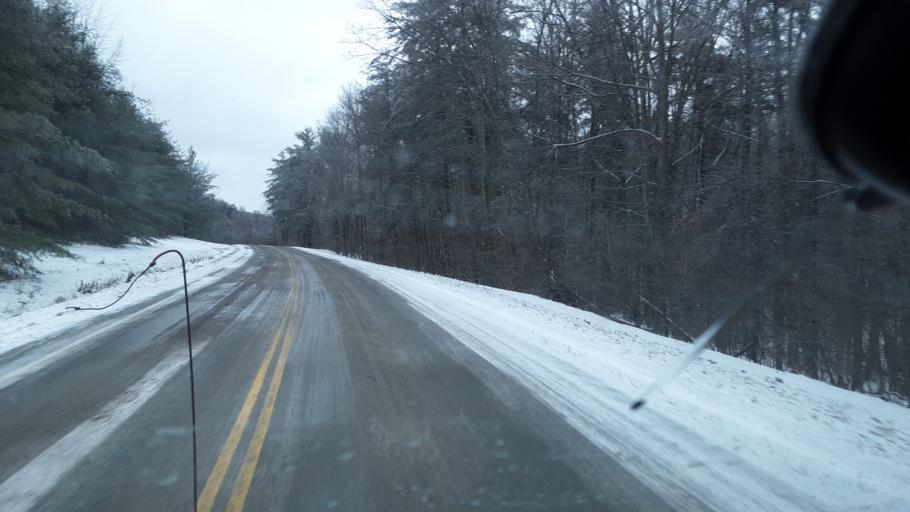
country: US
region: New York
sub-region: Allegany County
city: Friendship
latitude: 42.2443
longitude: -78.1467
